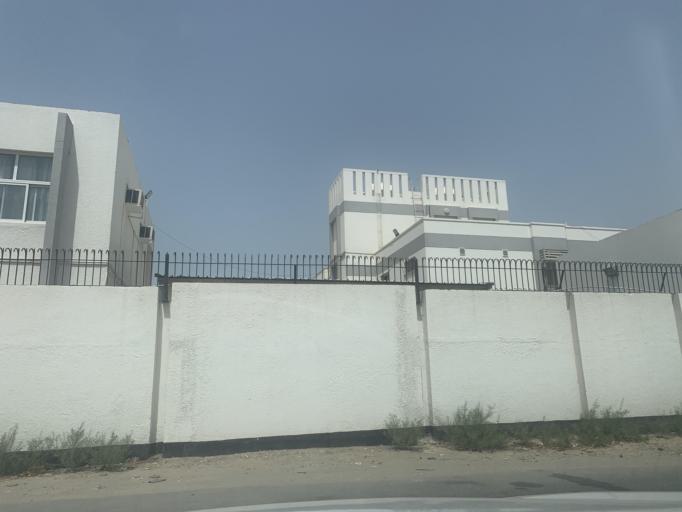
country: BH
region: Manama
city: Jidd Hafs
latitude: 26.2235
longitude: 50.4676
